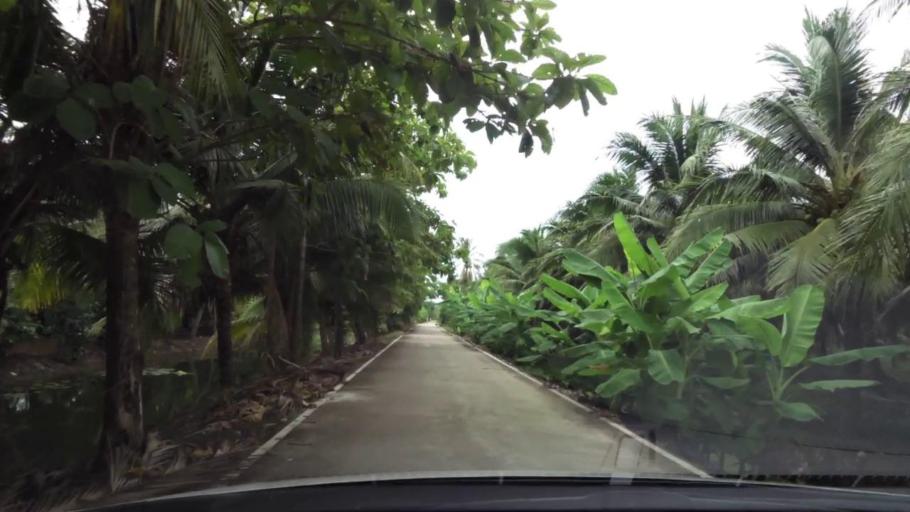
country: TH
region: Ratchaburi
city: Damnoen Saduak
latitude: 13.5558
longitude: 99.9832
